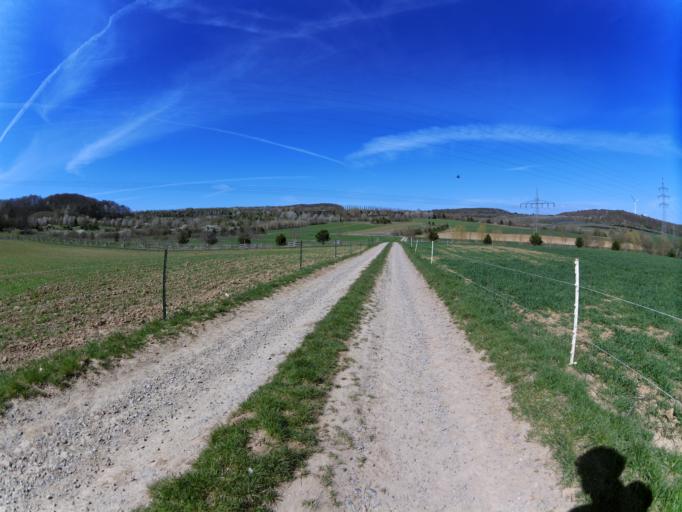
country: DE
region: Bavaria
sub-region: Regierungsbezirk Unterfranken
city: Hettstadt
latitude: 49.8115
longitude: 9.7969
